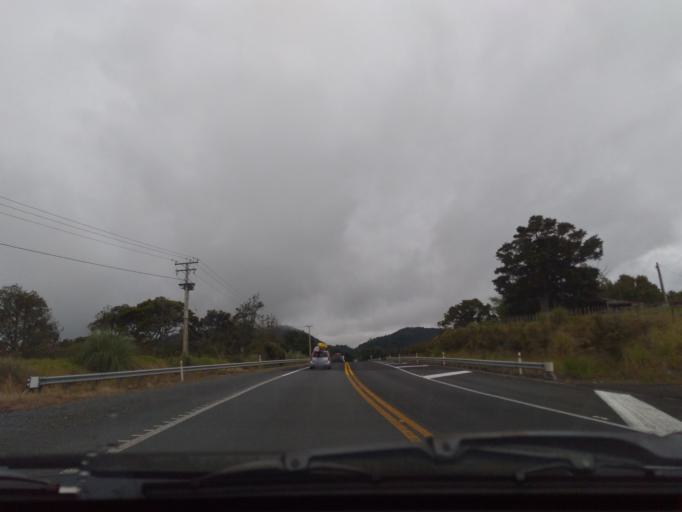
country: NZ
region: Auckland
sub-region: Auckland
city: Wellsford
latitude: -36.1413
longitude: 174.4328
